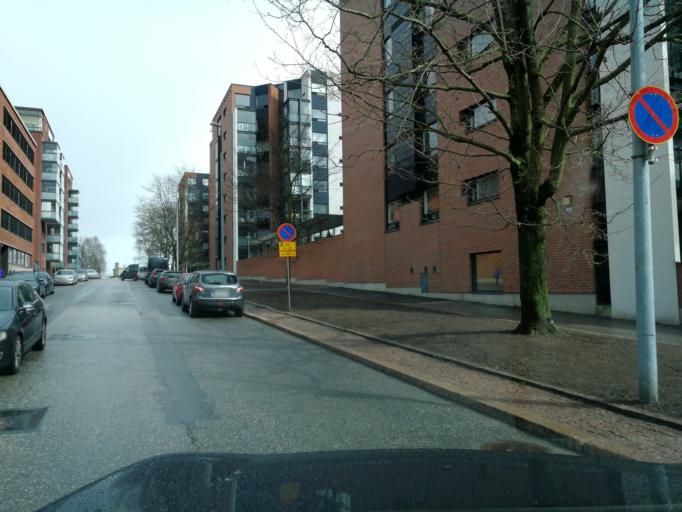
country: FI
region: Uusimaa
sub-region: Helsinki
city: Helsinki
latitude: 60.1507
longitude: 24.8829
